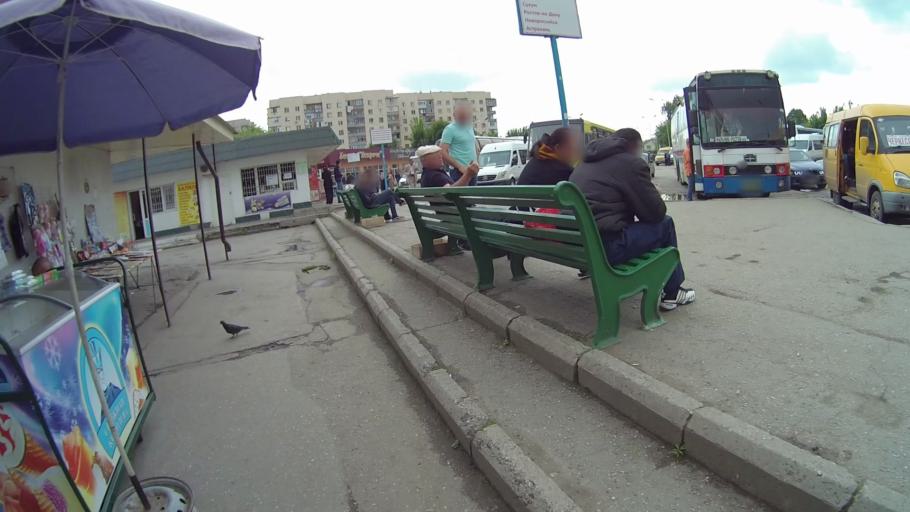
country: RU
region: Kabardino-Balkariya
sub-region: Gorod Nal'chik
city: Nal'chik
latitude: 43.5046
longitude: 43.6235
